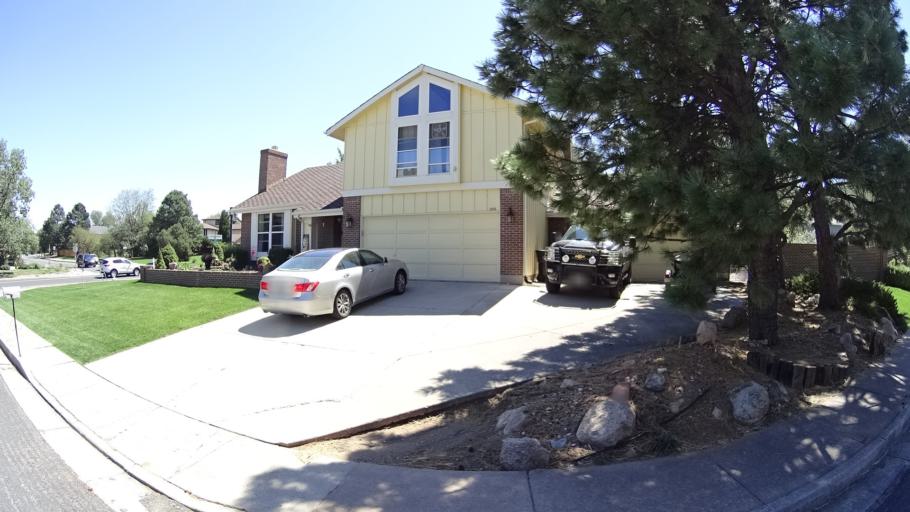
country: US
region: Colorado
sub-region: El Paso County
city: Colorado Springs
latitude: 38.7913
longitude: -104.8347
